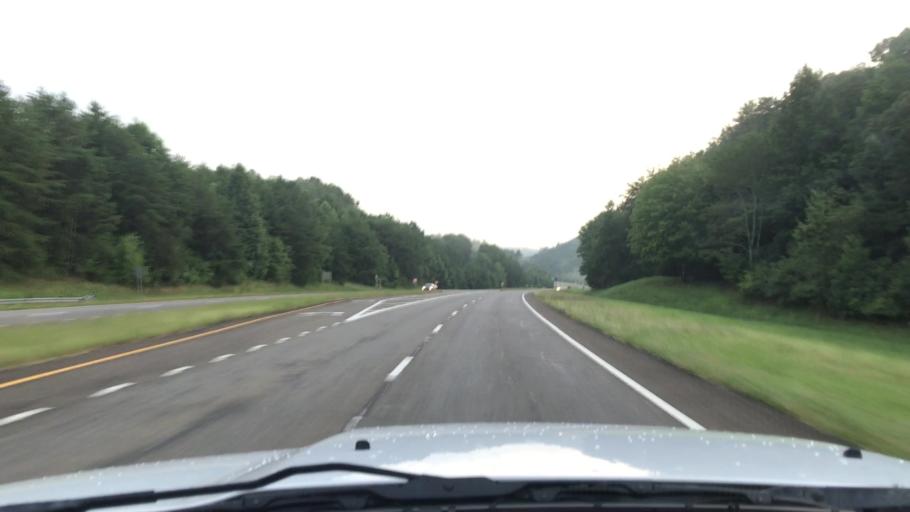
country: US
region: Georgia
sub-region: Gilmer County
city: Ellijay
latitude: 34.7074
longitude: -84.4573
